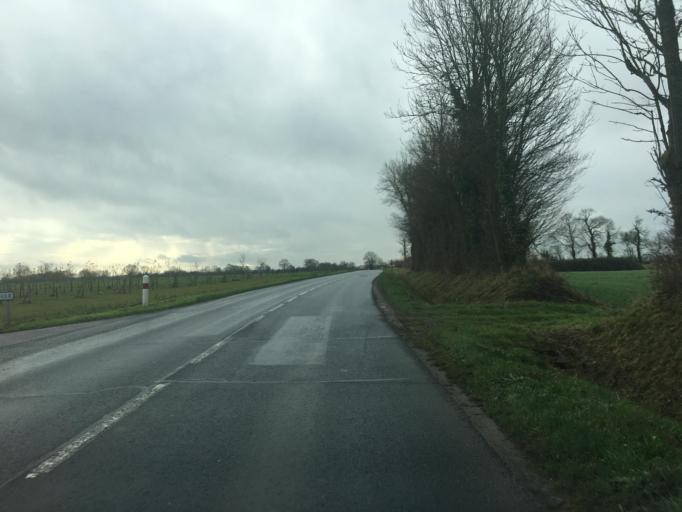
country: FR
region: Lower Normandy
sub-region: Departement du Calvados
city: Isigny-sur-Mer
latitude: 49.3449
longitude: -1.0761
